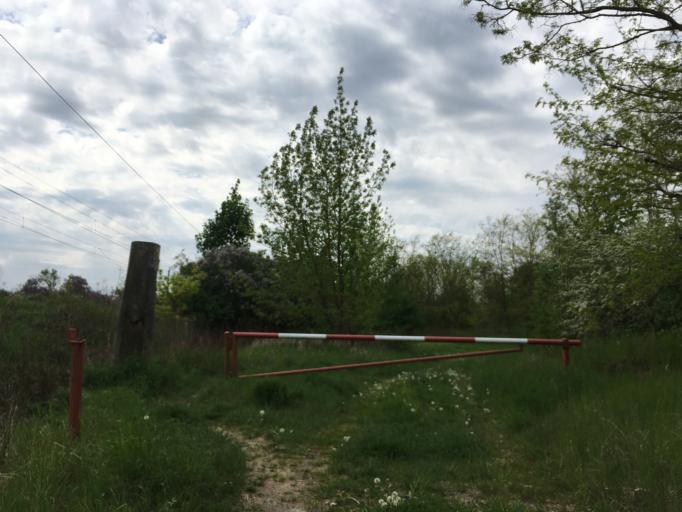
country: DE
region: Brandenburg
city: Bernau bei Berlin
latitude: 52.6930
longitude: 13.6111
